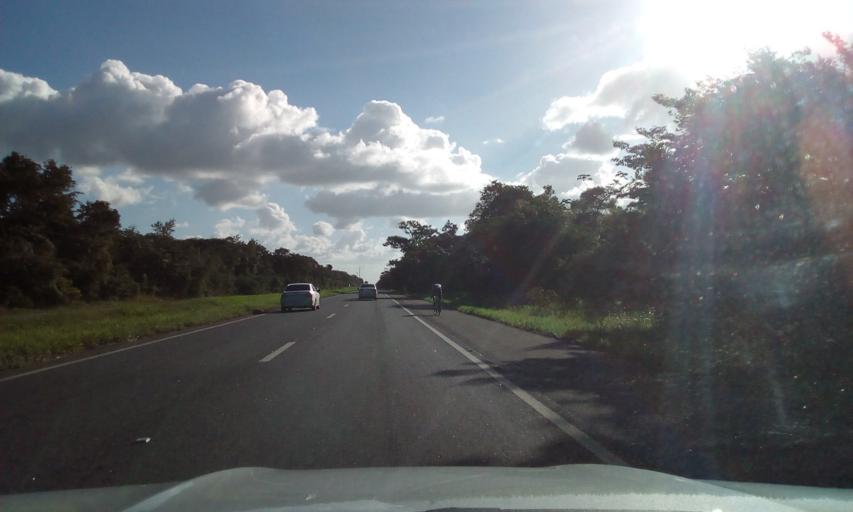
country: BR
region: Paraiba
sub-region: Cruz Do Espirito Santo
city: Cruz do Espirito Santo
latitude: -7.2010
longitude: -35.0888
